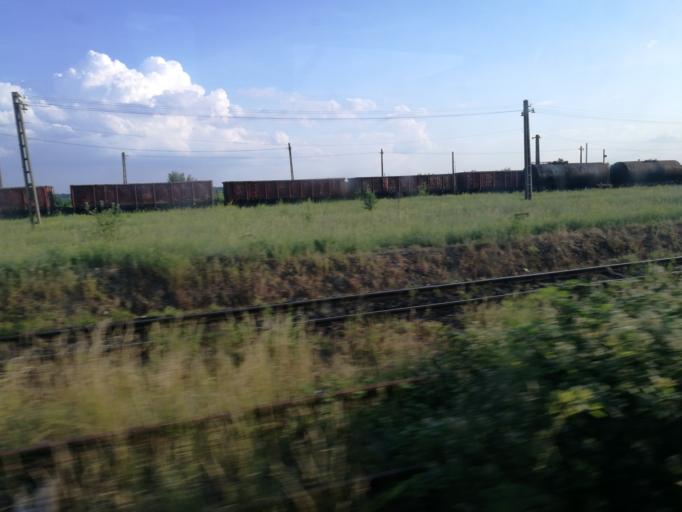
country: RO
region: Arges
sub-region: Oras Stefanesti
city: Golesti
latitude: 44.8353
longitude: 24.9739
